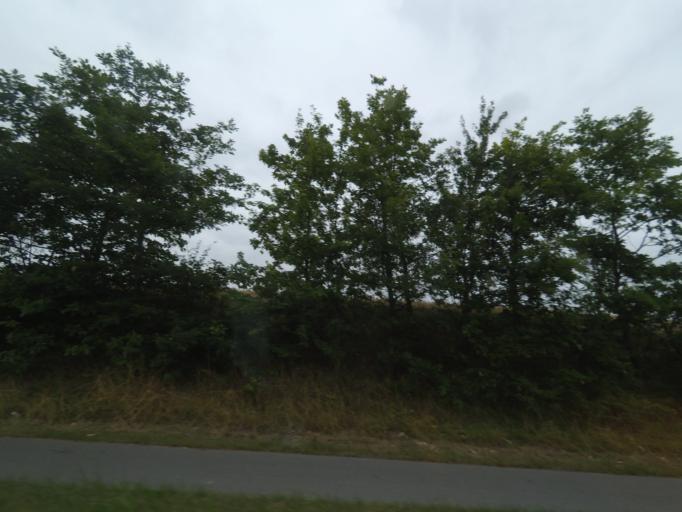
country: DK
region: South Denmark
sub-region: Nordfyns Kommune
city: Otterup
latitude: 55.5232
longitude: 10.4157
